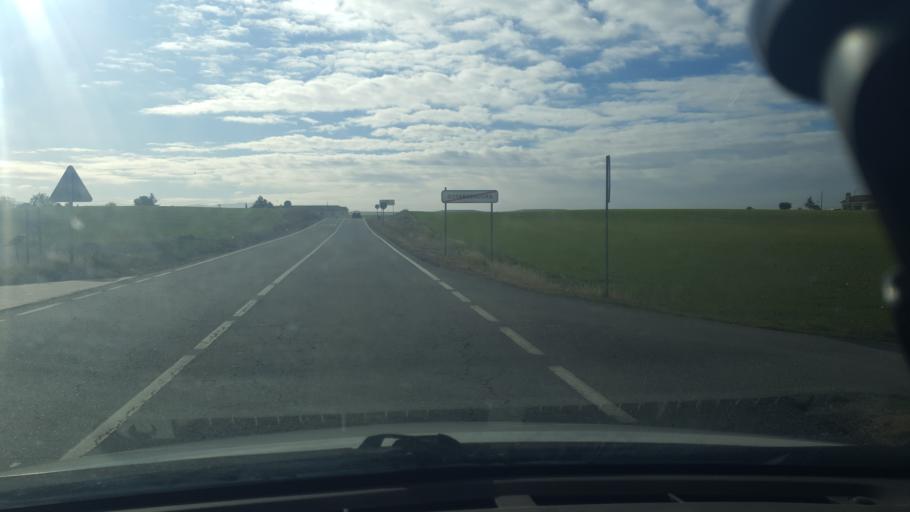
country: ES
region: Castille and Leon
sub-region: Provincia de Avila
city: Gotarrendura
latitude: 40.8243
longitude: -4.7390
